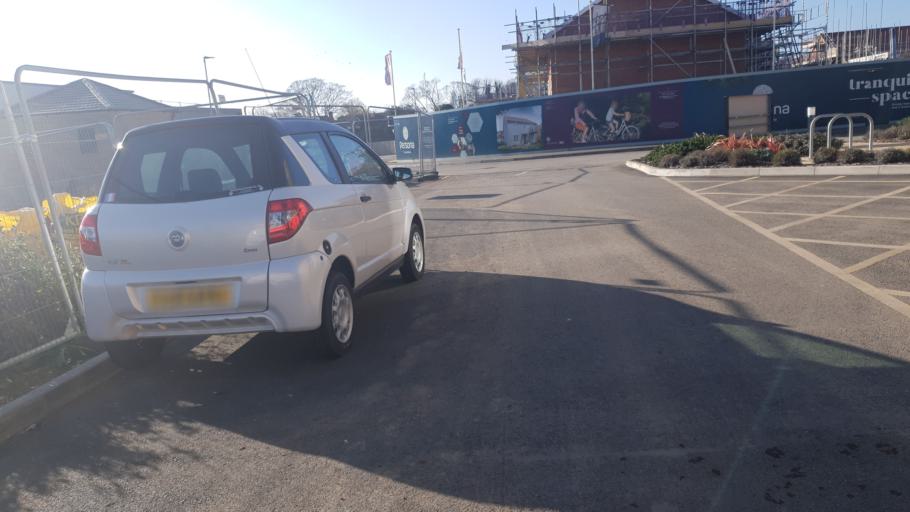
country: GB
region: England
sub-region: Essex
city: Walton-on-the-Naze
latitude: 51.8508
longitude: 1.2663
